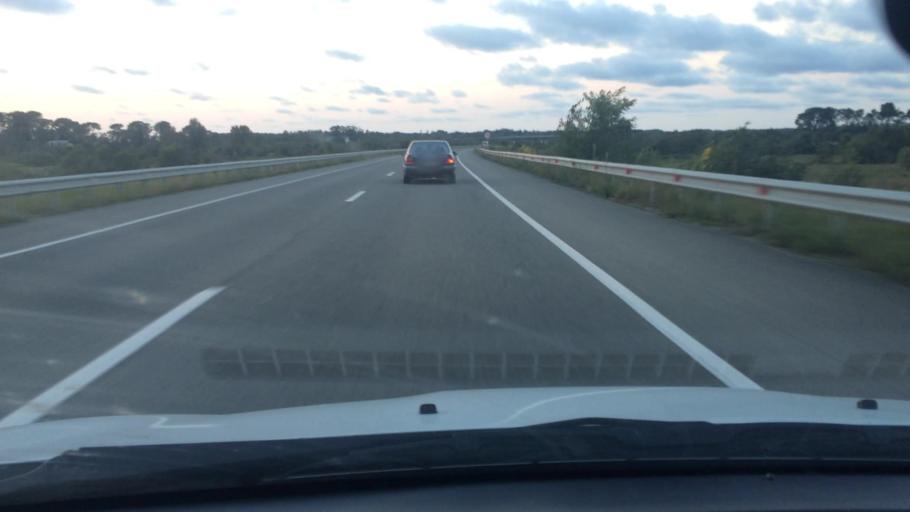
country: GE
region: Guria
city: Urek'i
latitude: 41.9121
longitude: 41.7807
